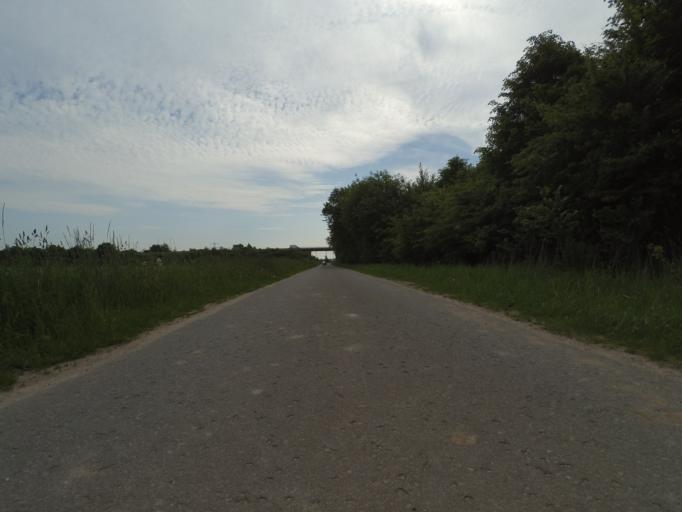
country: DE
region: Lower Saxony
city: Lehrte
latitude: 52.3542
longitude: 9.9721
